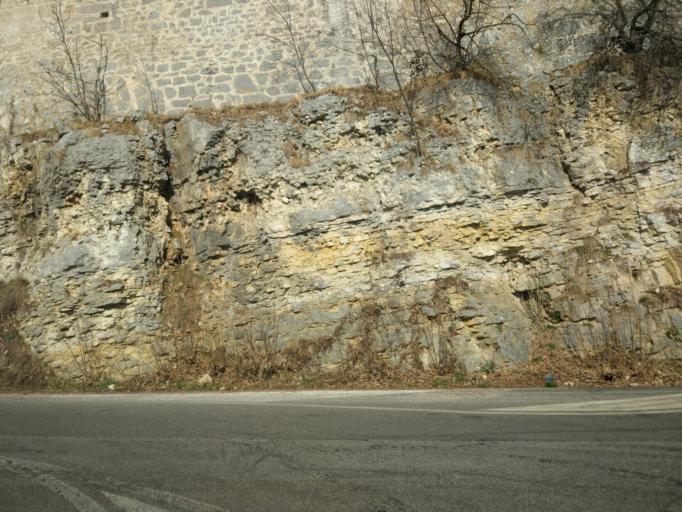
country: IT
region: Veneto
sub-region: Provincia di Verona
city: Bosco Chiesanuova
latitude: 45.6266
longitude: 11.0342
